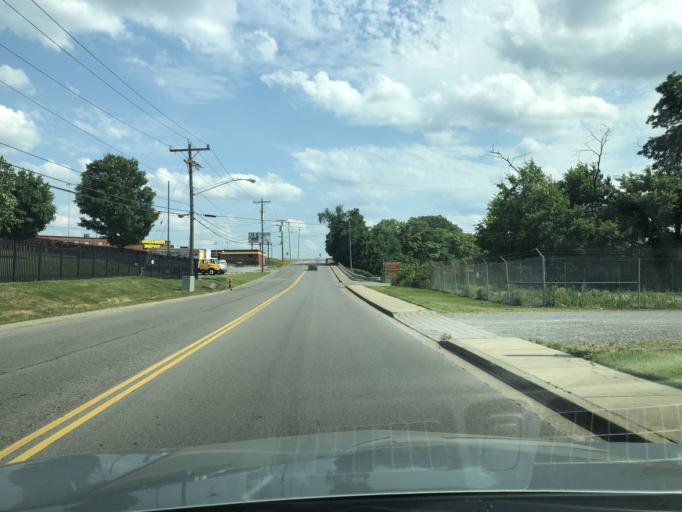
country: US
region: Tennessee
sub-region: Davidson County
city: Oak Hill
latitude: 36.0965
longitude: -86.7591
